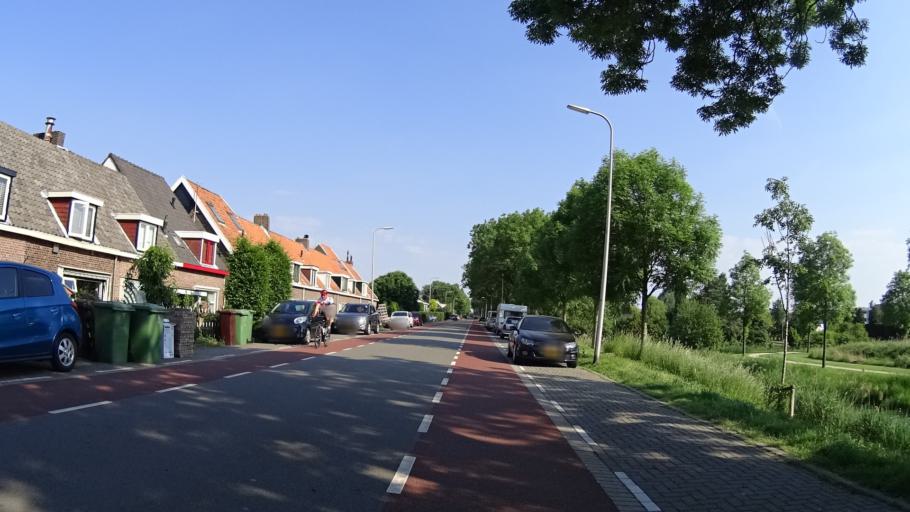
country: NL
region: South Holland
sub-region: Gemeente Barendrecht
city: Barendrecht
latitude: 51.8645
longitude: 4.5594
